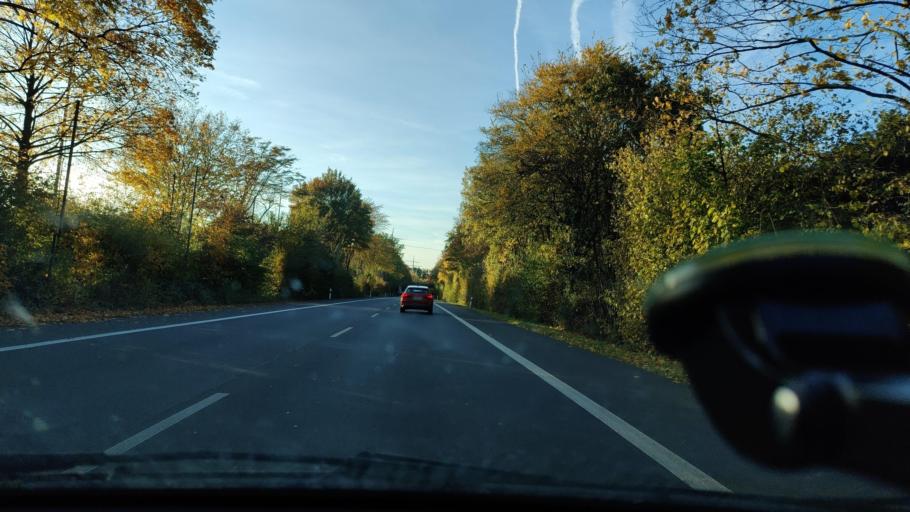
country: DE
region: North Rhine-Westphalia
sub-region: Regierungsbezirk Dusseldorf
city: Monchengladbach
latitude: 51.2280
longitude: 6.4711
